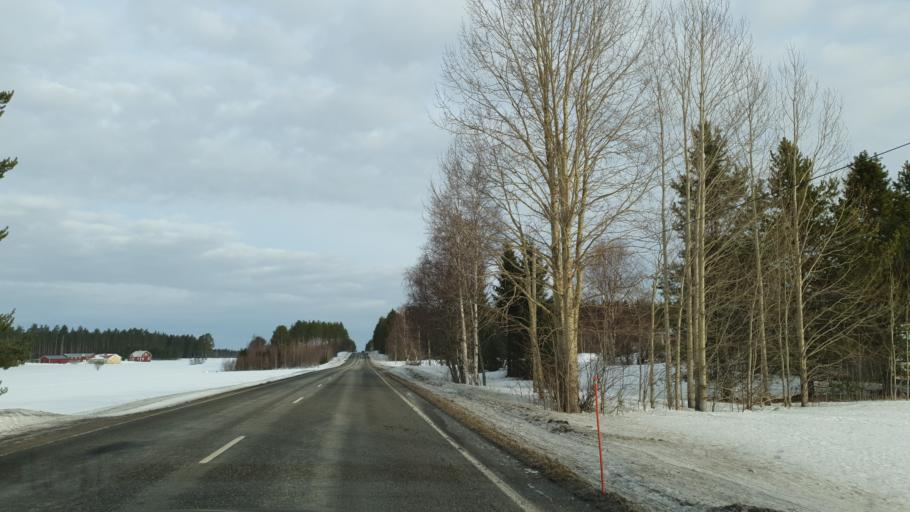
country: FI
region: Kainuu
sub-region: Kajaani
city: Vuokatti
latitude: 64.1771
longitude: 28.1962
